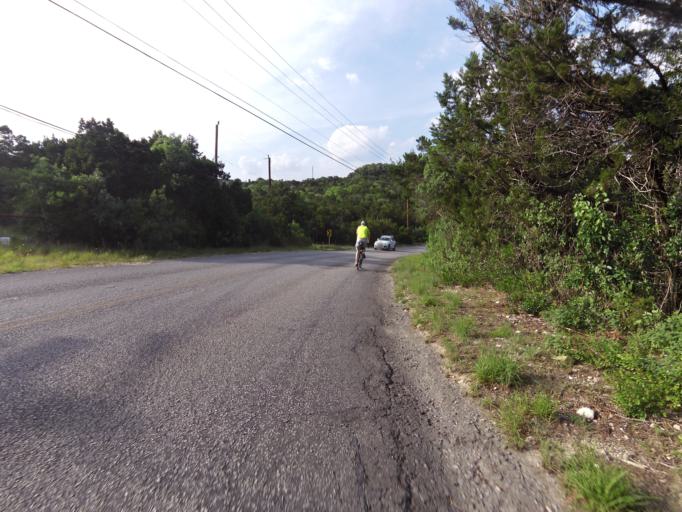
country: US
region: Texas
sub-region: Bexar County
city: Cross Mountain
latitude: 29.6574
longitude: -98.6350
